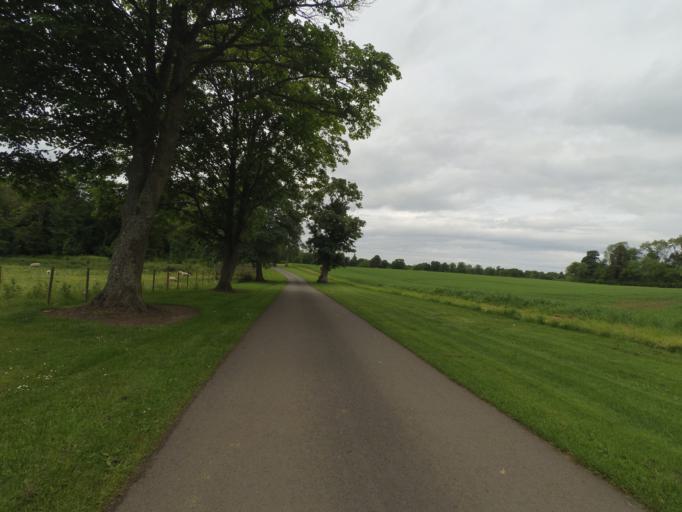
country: GB
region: Scotland
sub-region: East Lothian
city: Pencaitland
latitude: 55.9129
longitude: -2.8938
